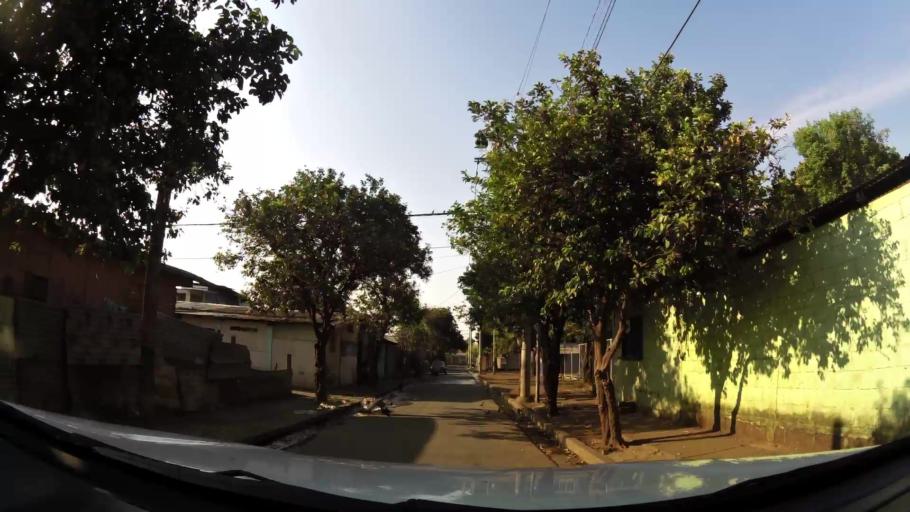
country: NI
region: Managua
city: Managua
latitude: 12.1250
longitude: -86.2490
